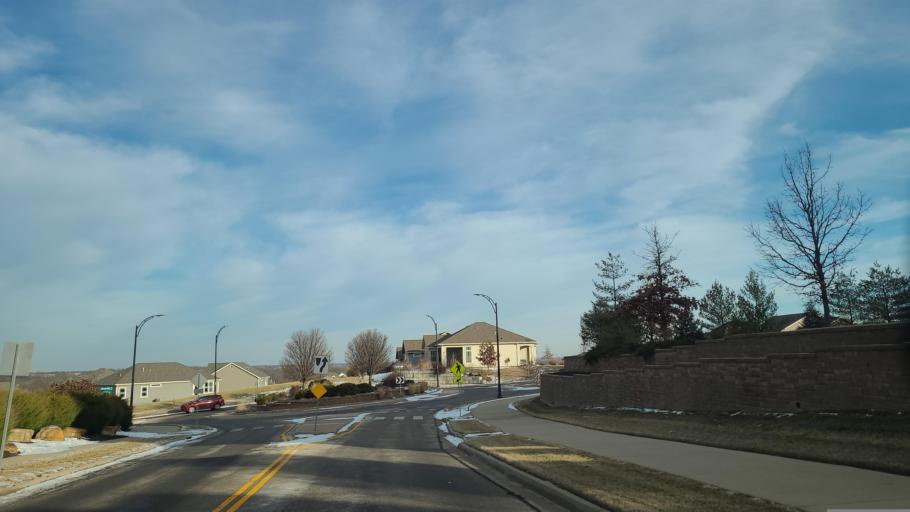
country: US
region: Kansas
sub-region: Douglas County
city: Lawrence
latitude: 38.9745
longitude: -95.3208
